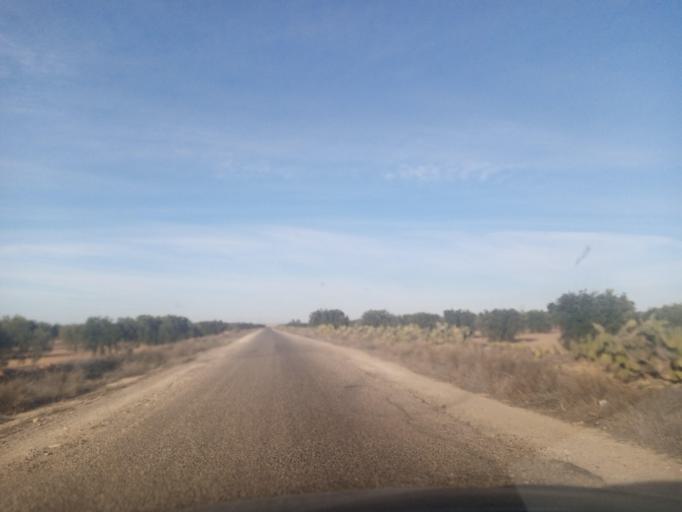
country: TN
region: Safaqis
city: Bi'r `Ali Bin Khalifah
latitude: 34.8586
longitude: 10.1642
